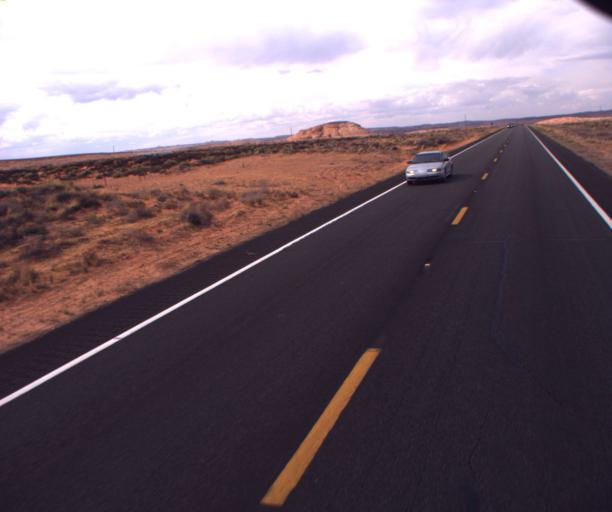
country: US
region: Arizona
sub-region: Apache County
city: Many Farms
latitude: 36.9276
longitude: -109.6192
